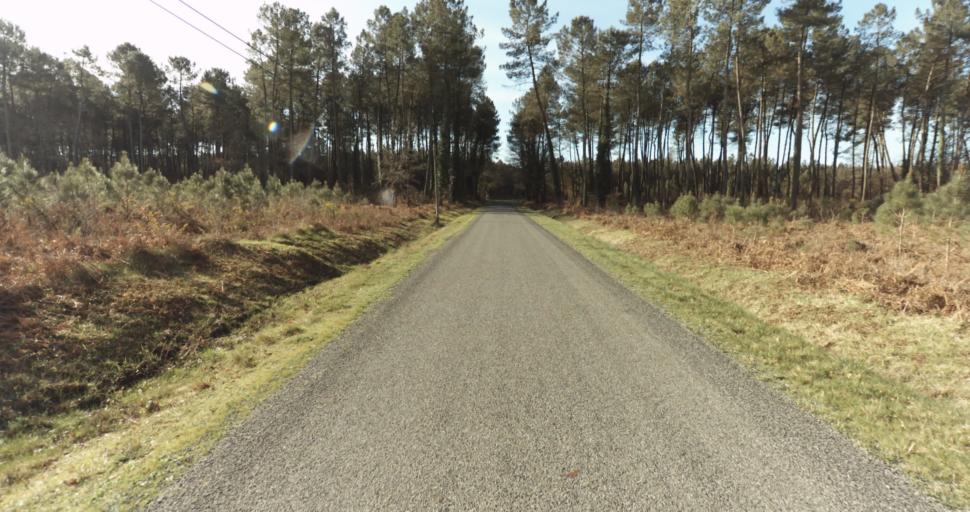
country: FR
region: Aquitaine
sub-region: Departement des Landes
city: Sarbazan
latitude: 44.0055
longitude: -0.2316
